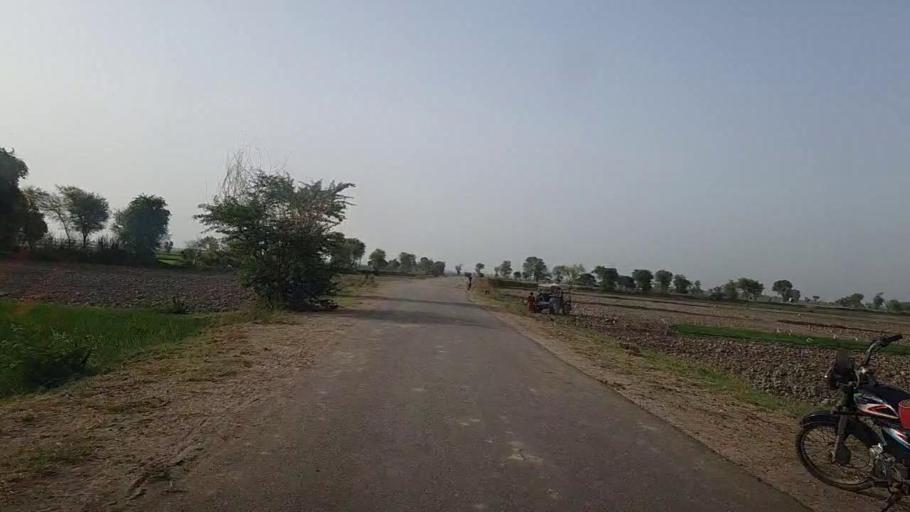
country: PK
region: Sindh
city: Khairpur Nathan Shah
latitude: 27.1051
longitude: 67.7936
